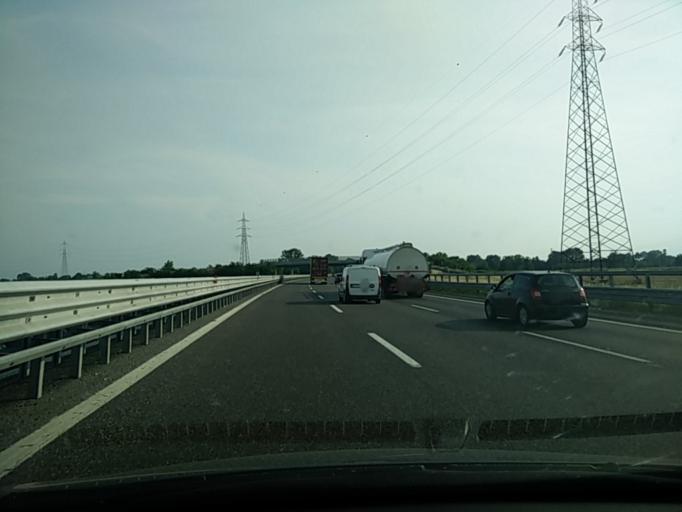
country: IT
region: Lombardy
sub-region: Citta metropolitana di Milano
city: Zibido San Giacomo
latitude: 45.3766
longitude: 9.1312
